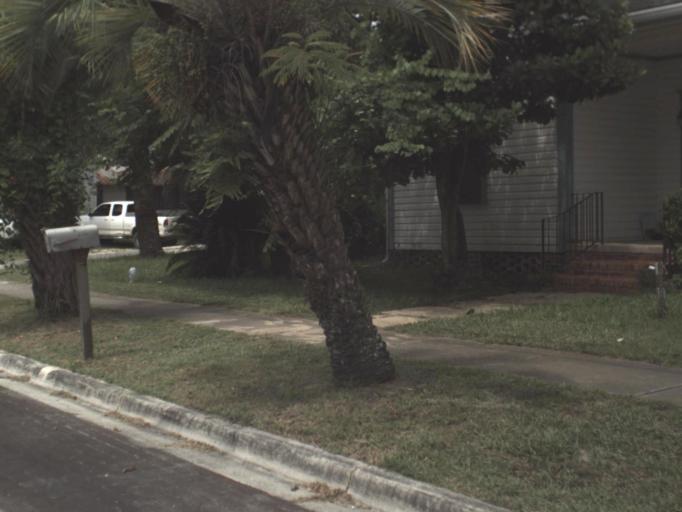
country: US
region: Florida
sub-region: Alachua County
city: High Springs
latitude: 29.8242
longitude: -82.5988
